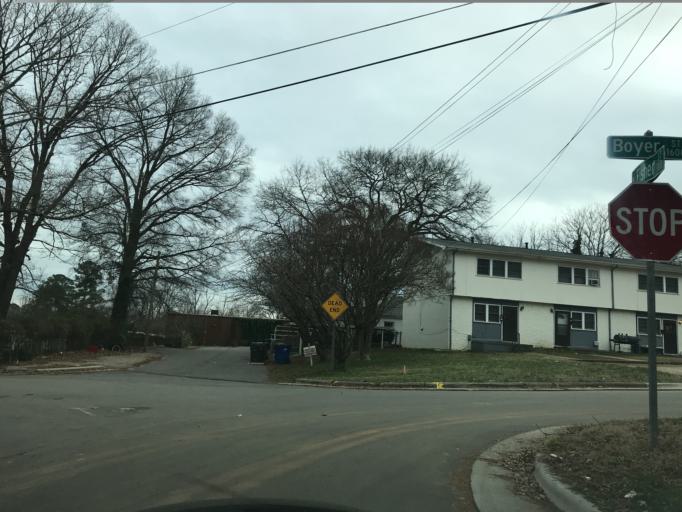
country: US
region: North Carolina
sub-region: Wake County
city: Raleigh
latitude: 35.7812
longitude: -78.6150
